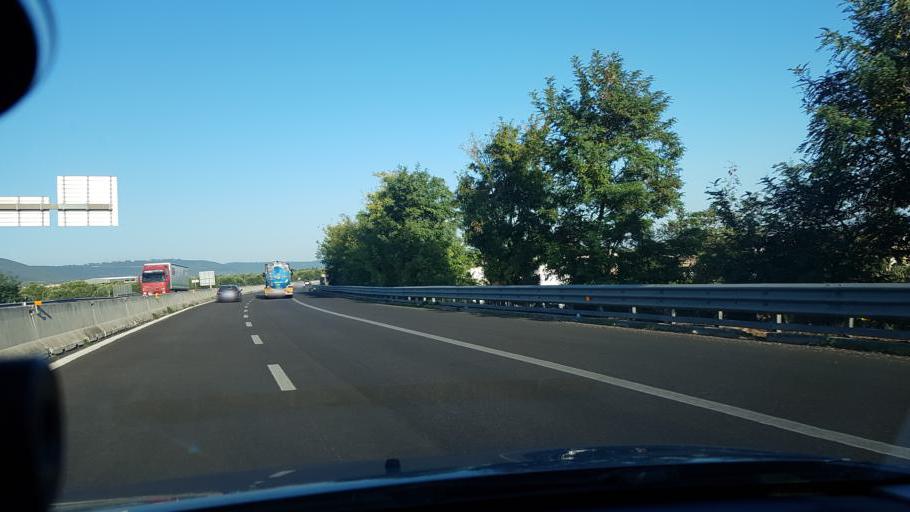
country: IT
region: Apulia
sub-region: Provincia di Brindisi
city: Fasano
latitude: 40.8417
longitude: 17.3685
